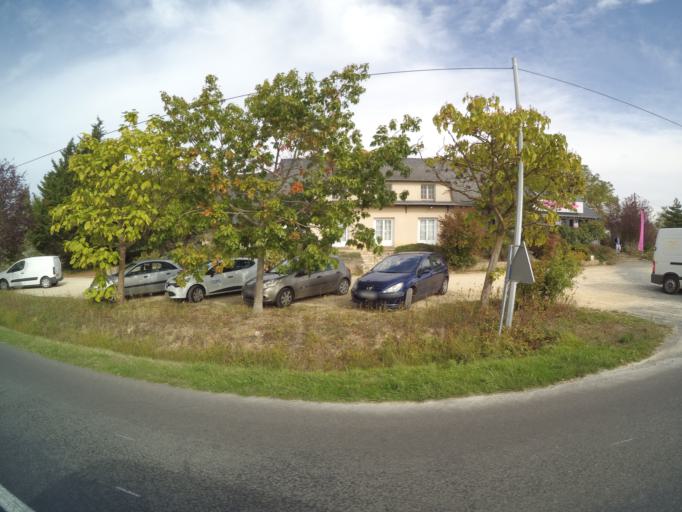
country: FR
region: Pays de la Loire
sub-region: Departement de Maine-et-Loire
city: Martigne-Briand
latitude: 47.2076
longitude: -0.4687
